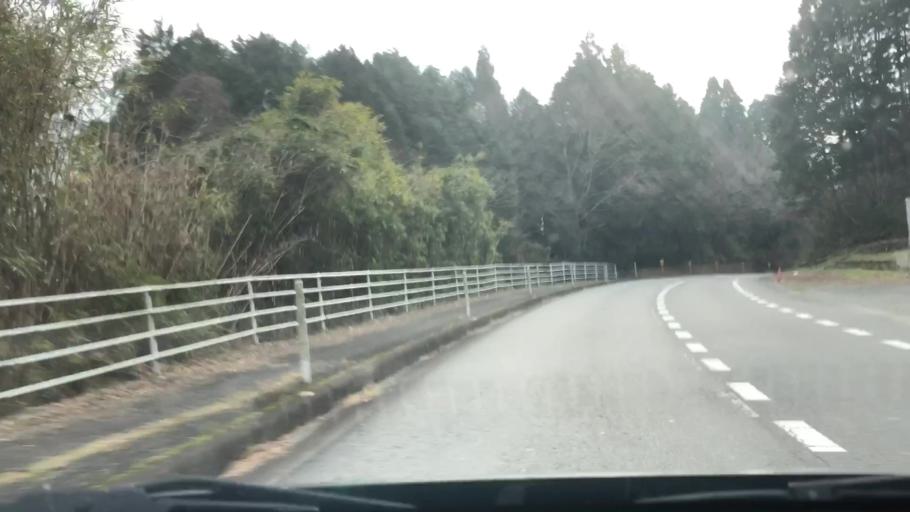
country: JP
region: Oita
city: Takedamachi
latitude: 32.9781
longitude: 131.5586
